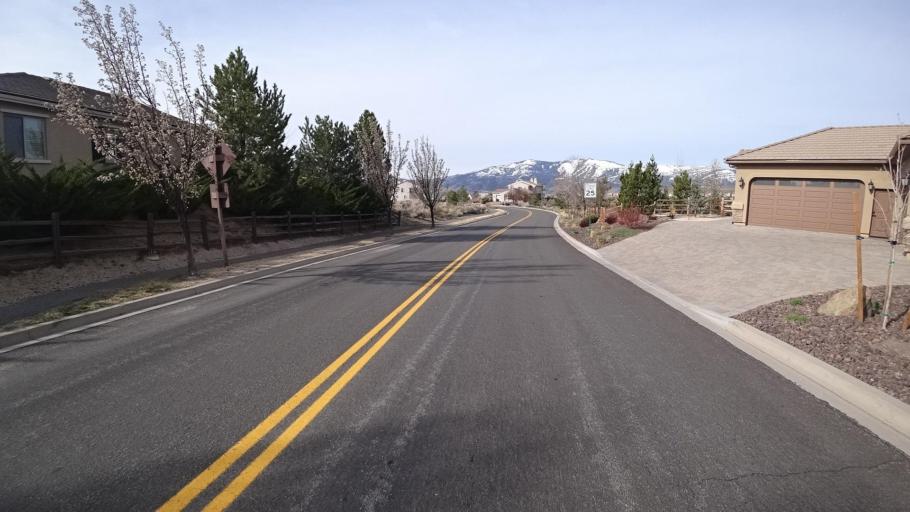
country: US
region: Nevada
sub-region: Washoe County
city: Mogul
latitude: 39.5360
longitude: -119.9370
